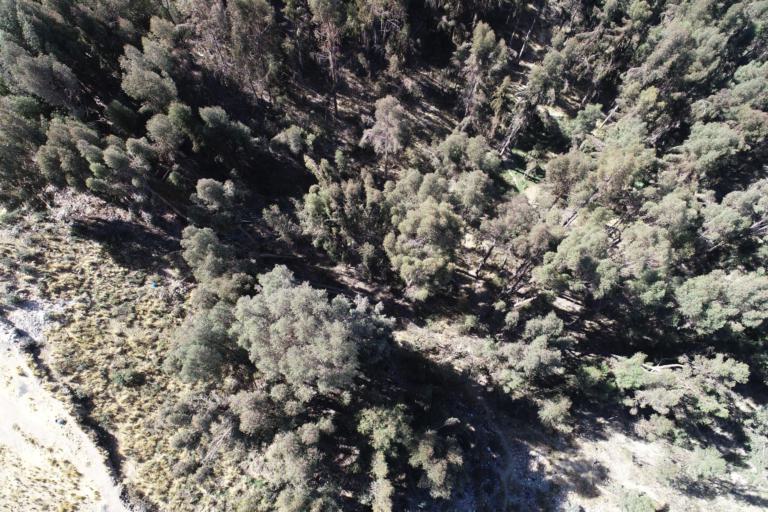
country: BO
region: La Paz
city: La Paz
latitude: -16.5405
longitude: -68.1561
